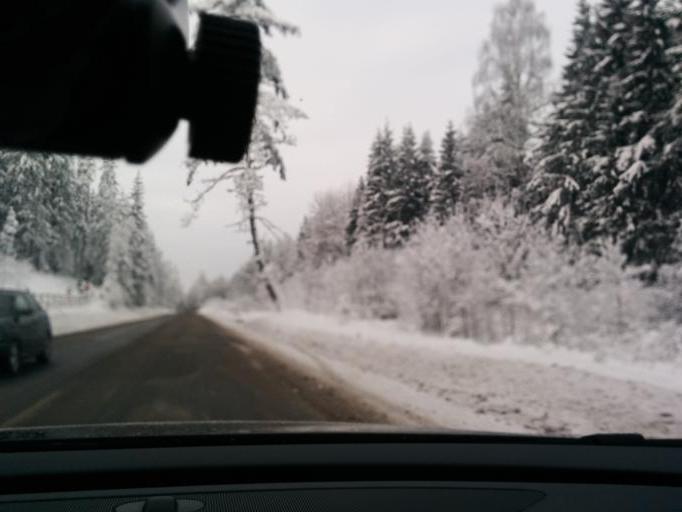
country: LV
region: Ogre
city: Ogre
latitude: 56.8290
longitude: 24.5931
